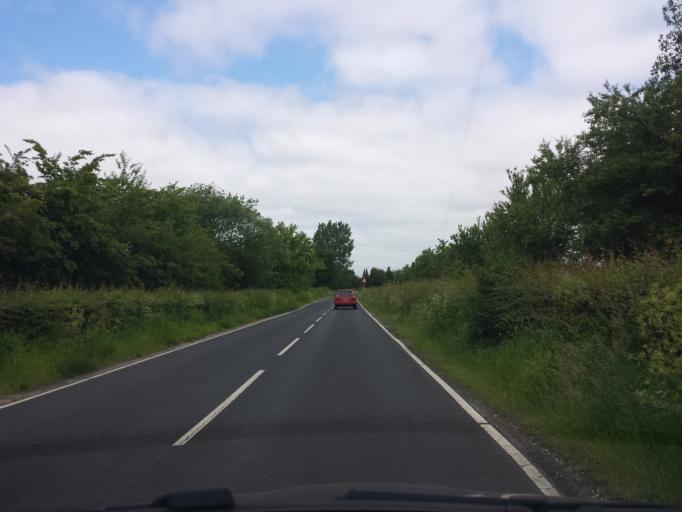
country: DK
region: Capital Region
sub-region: Glostrup Kommune
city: Glostrup
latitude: 55.7079
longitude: 12.3977
